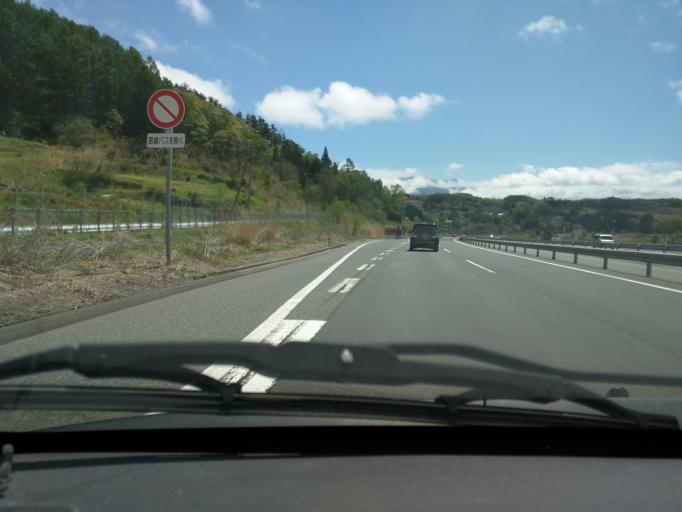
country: JP
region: Nagano
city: Iiyama
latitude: 36.8027
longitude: 138.3136
